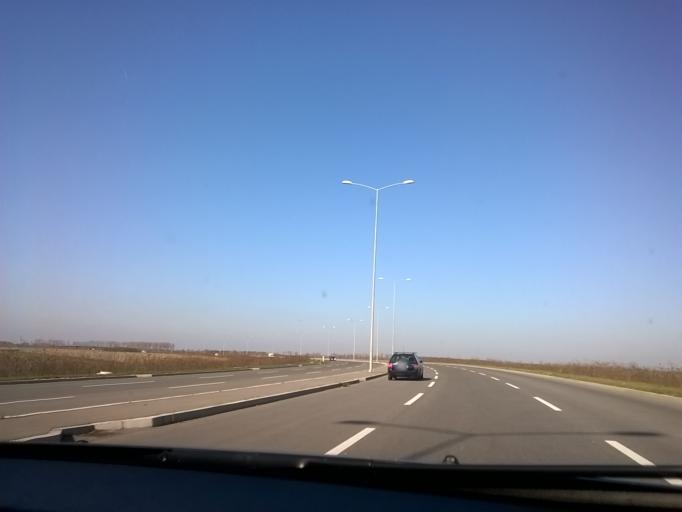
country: RS
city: Ovca
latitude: 44.9110
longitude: 20.5102
